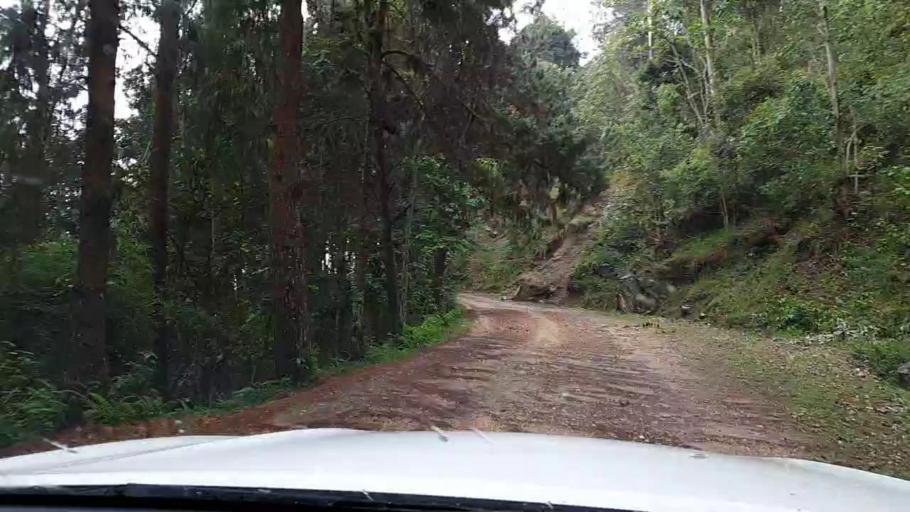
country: RW
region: Western Province
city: Cyangugu
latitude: -2.5594
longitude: 28.9909
